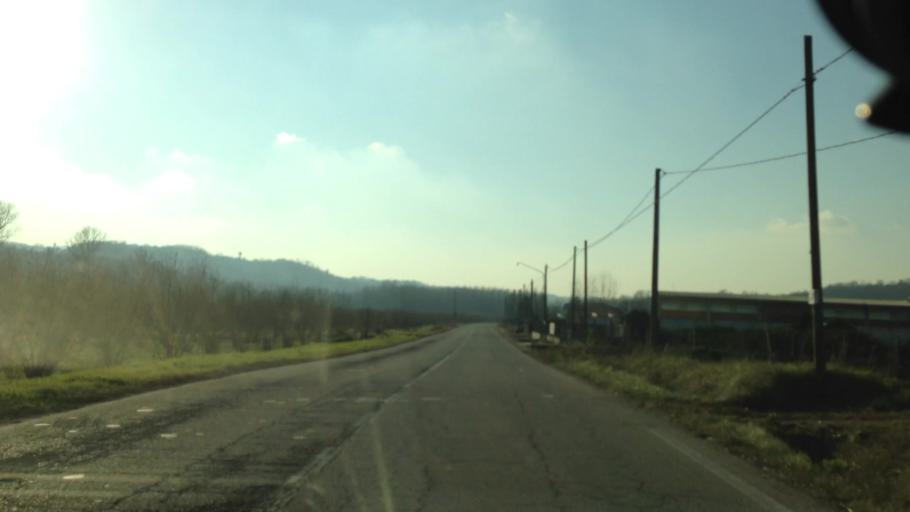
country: IT
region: Piedmont
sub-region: Provincia di Asti
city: Cortiglione
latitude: 44.8380
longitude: 8.3839
